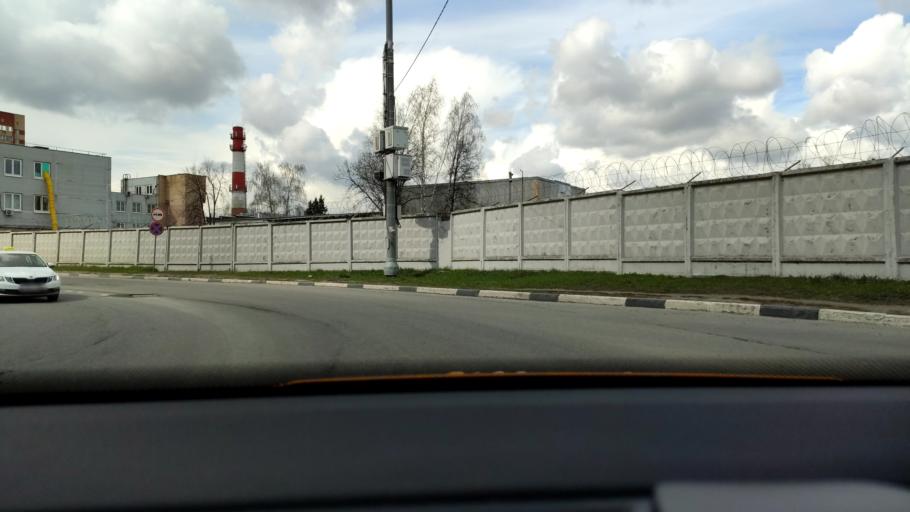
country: RU
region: Moskovskaya
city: Zheleznodorozhnyy
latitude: 55.7486
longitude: 38.0340
